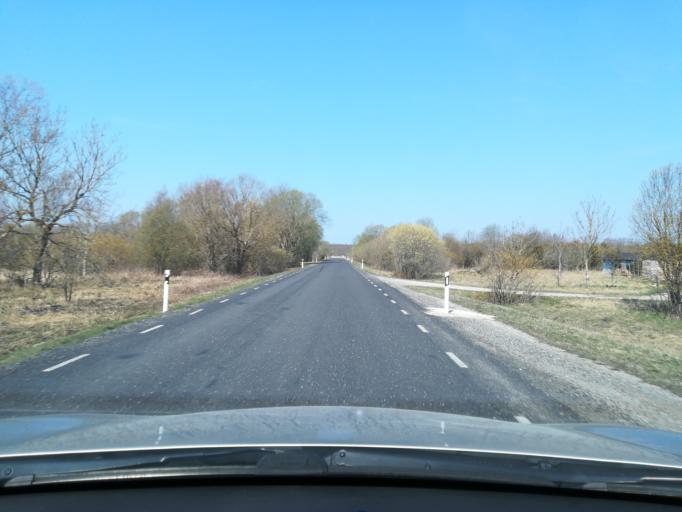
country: EE
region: Harju
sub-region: Harku vald
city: Tabasalu
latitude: 59.4343
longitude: 24.4021
